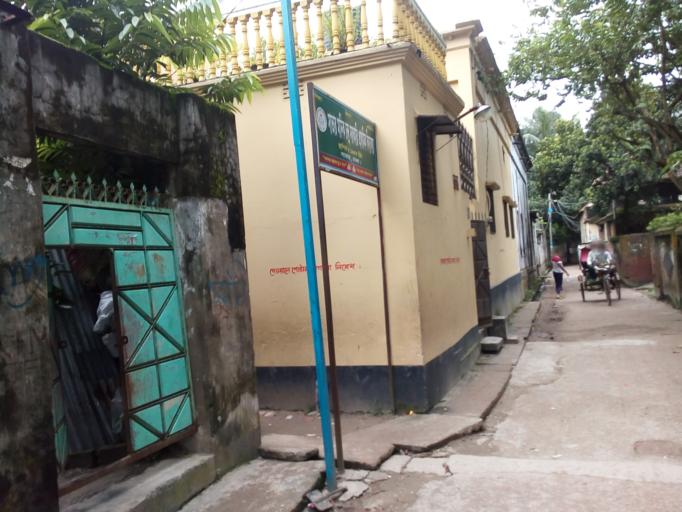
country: BD
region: Dhaka
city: Tungi
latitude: 23.8417
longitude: 90.2484
